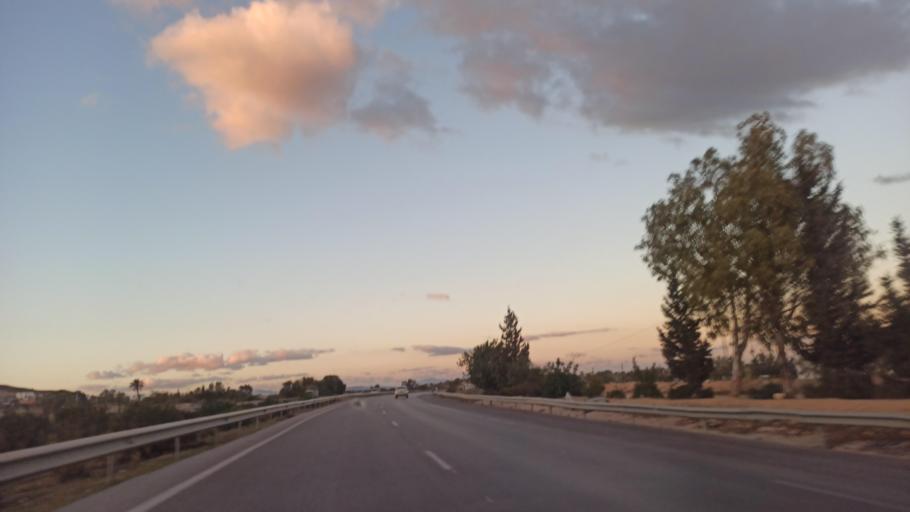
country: TN
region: Susah
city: Harqalah
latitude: 36.2314
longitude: 10.4131
